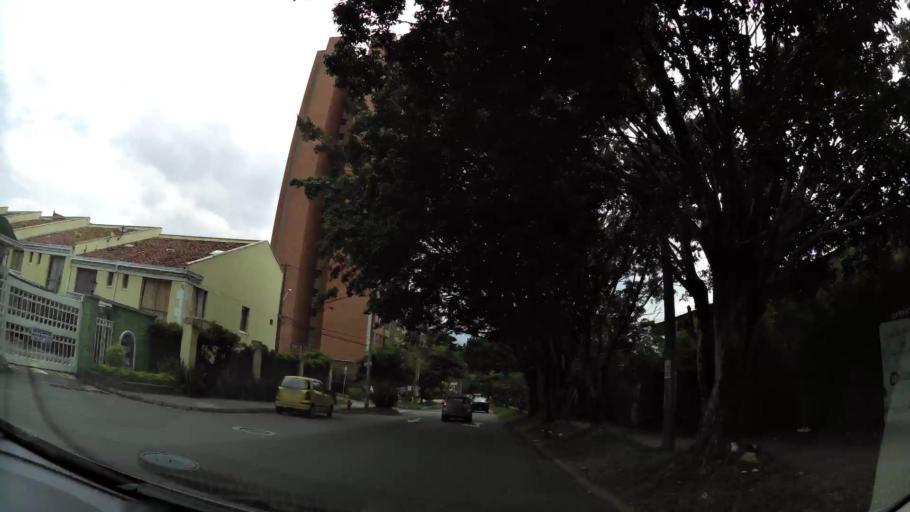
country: CO
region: Antioquia
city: Medellin
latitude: 6.2688
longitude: -75.5982
